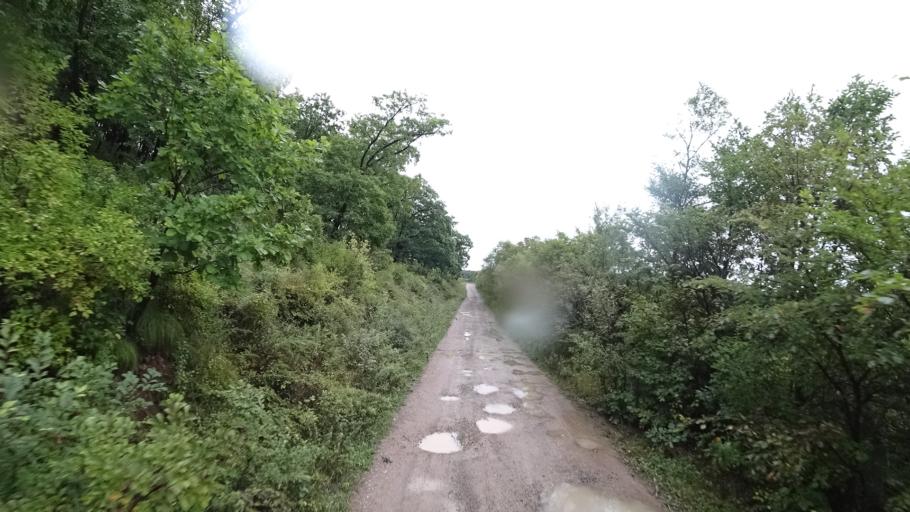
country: RU
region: Primorskiy
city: Monastyrishche
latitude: 44.2602
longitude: 132.4075
